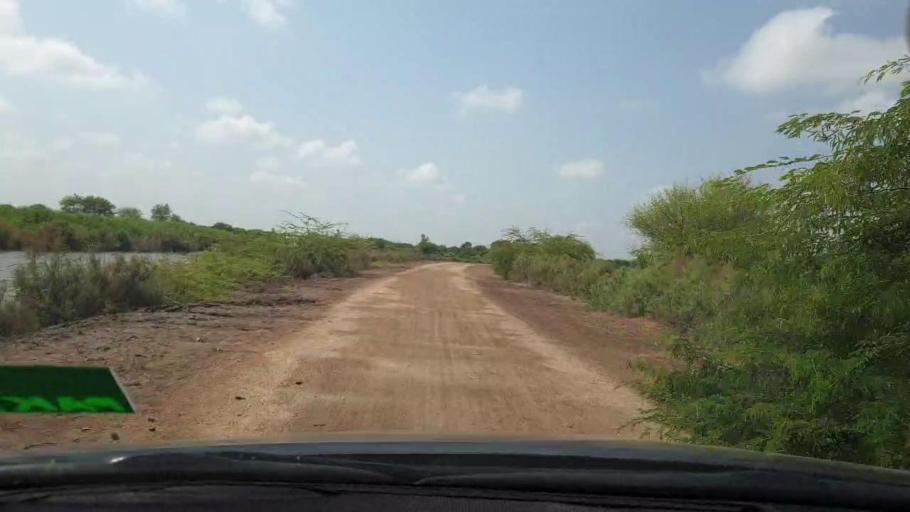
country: PK
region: Sindh
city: Tando Bago
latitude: 24.9321
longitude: 69.0448
